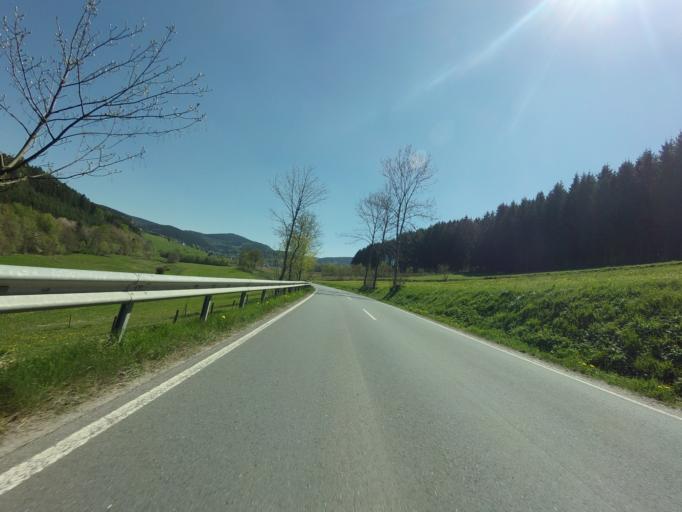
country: DE
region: North Rhine-Westphalia
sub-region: Regierungsbezirk Arnsberg
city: Kirchhundem
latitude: 51.0834
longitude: 8.1568
